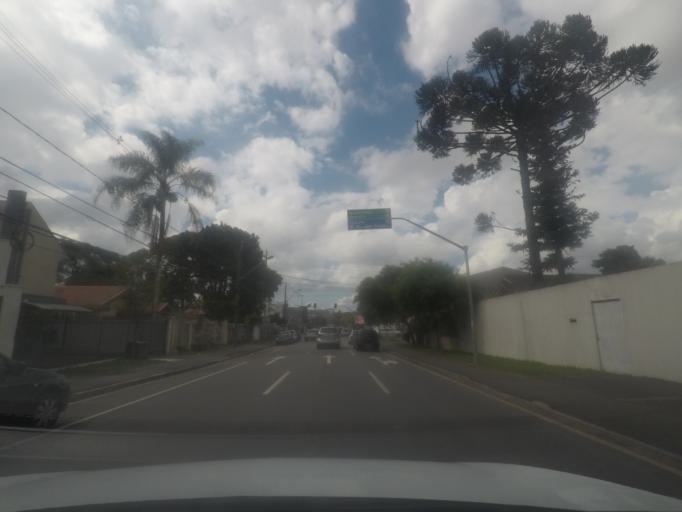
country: BR
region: Parana
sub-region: Curitiba
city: Curitiba
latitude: -25.4484
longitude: -49.2551
